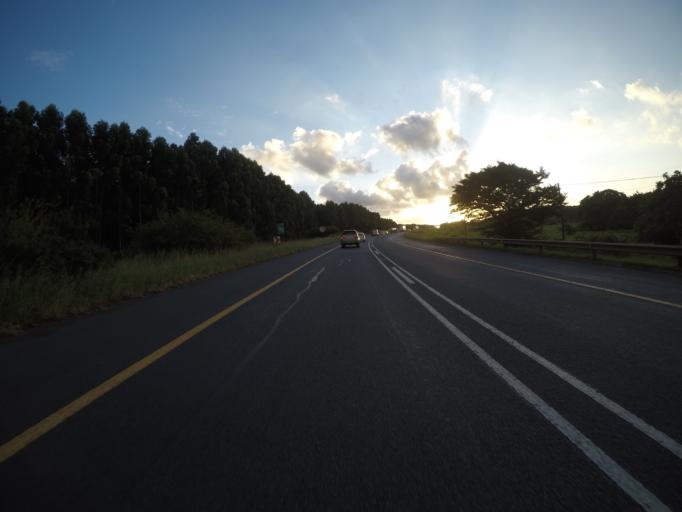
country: ZA
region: KwaZulu-Natal
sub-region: uThungulu District Municipality
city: Richards Bay
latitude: -28.6924
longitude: 32.0355
